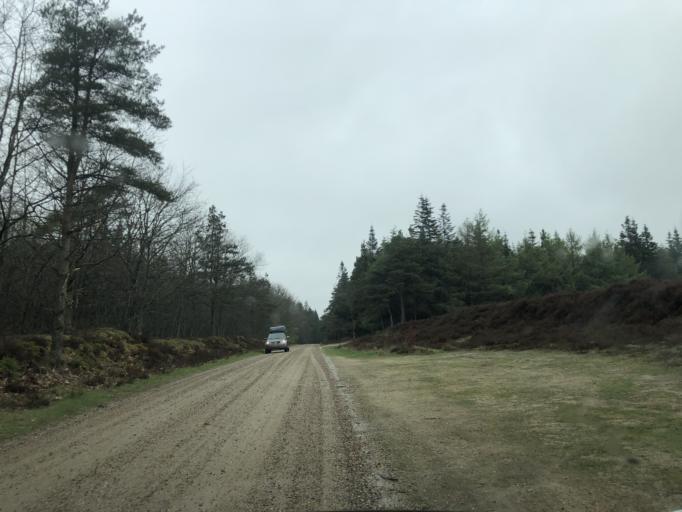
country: DK
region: Central Jutland
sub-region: Lemvig Kommune
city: Lemvig
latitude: 56.4758
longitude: 8.3762
